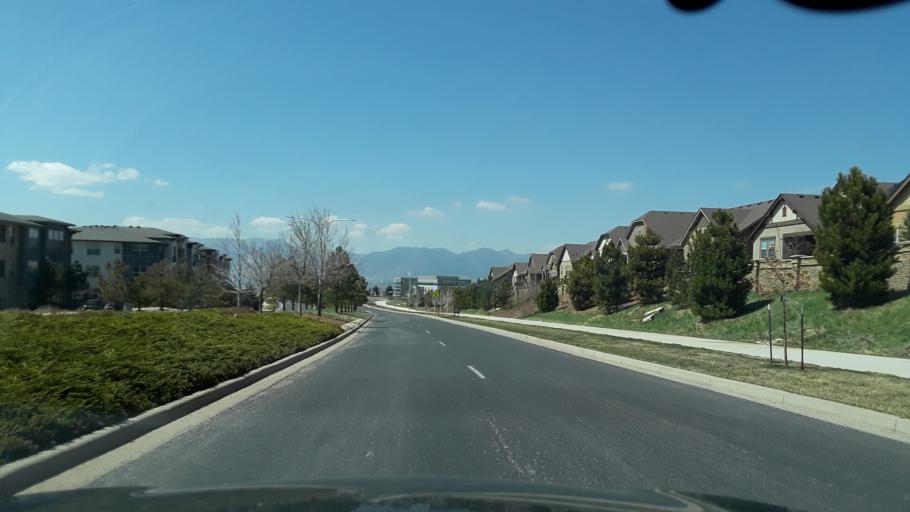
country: US
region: Colorado
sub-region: El Paso County
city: Black Forest
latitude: 38.9760
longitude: -104.7412
